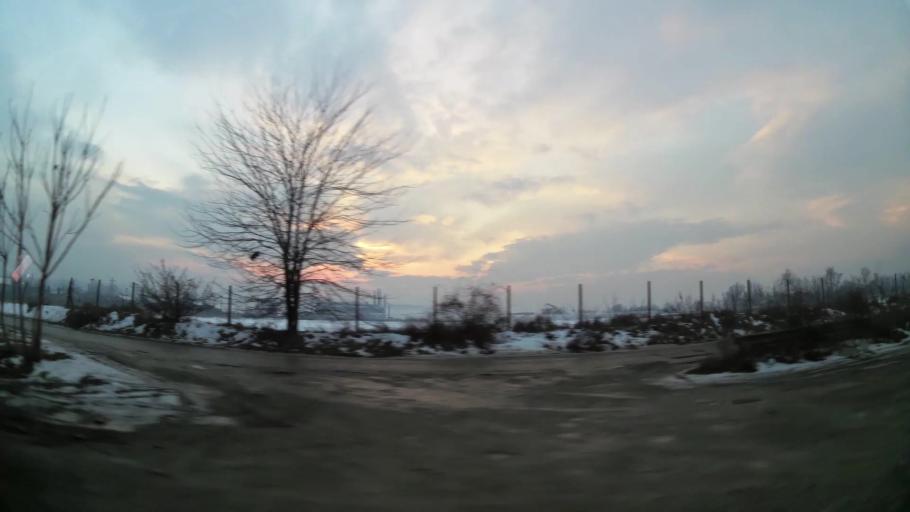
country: MK
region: Suto Orizari
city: Suto Orizare
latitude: 42.0240
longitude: 21.4091
